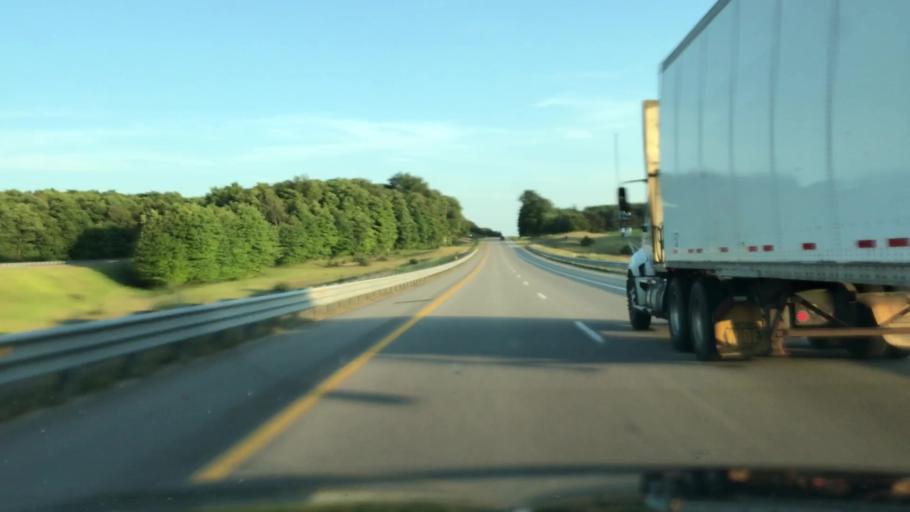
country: US
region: Michigan
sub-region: Osceola County
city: Reed City
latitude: 43.8571
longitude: -85.5345
